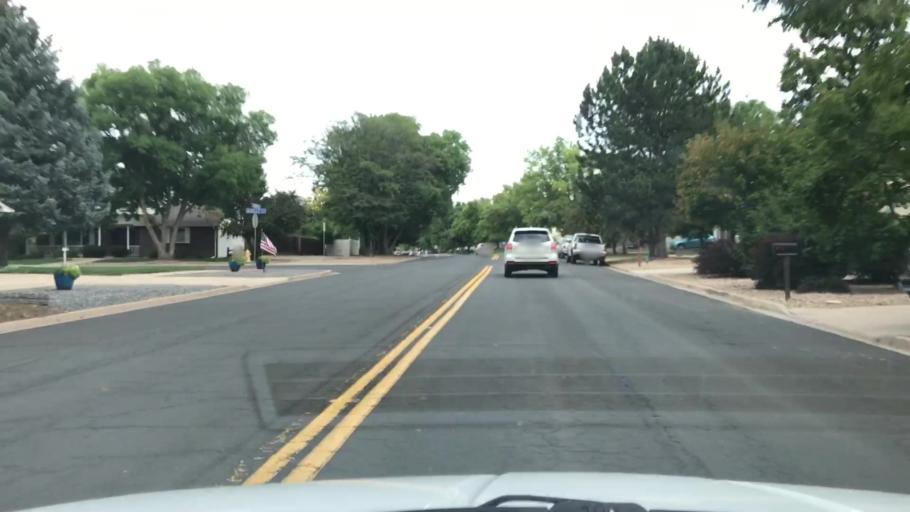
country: US
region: Colorado
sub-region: Broomfield County
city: Broomfield
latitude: 39.9329
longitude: -105.0805
